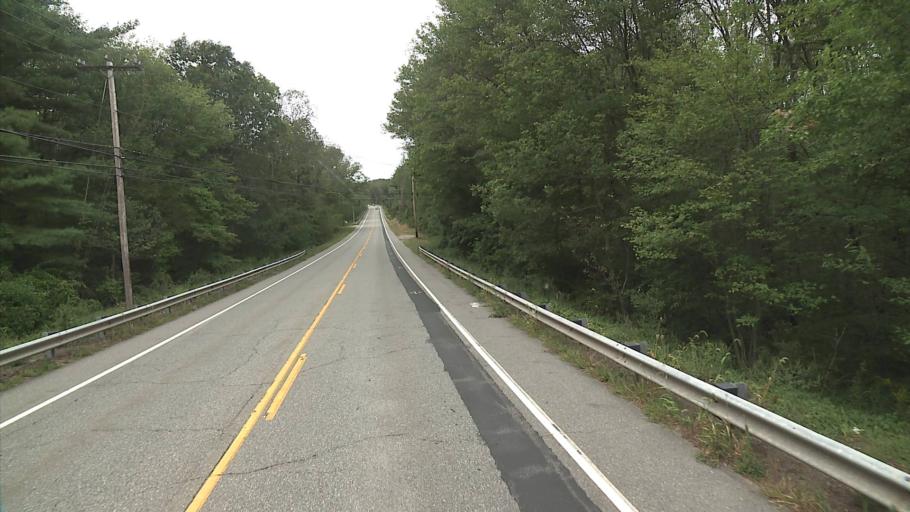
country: US
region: Connecticut
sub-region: Tolland County
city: Hebron
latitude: 41.6735
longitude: -72.3936
